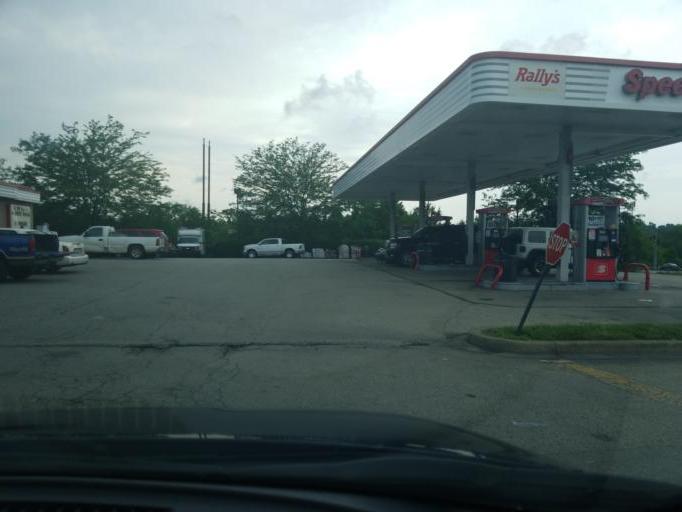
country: US
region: Kentucky
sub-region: Oldham County
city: La Grange
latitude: 38.3975
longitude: -85.3720
